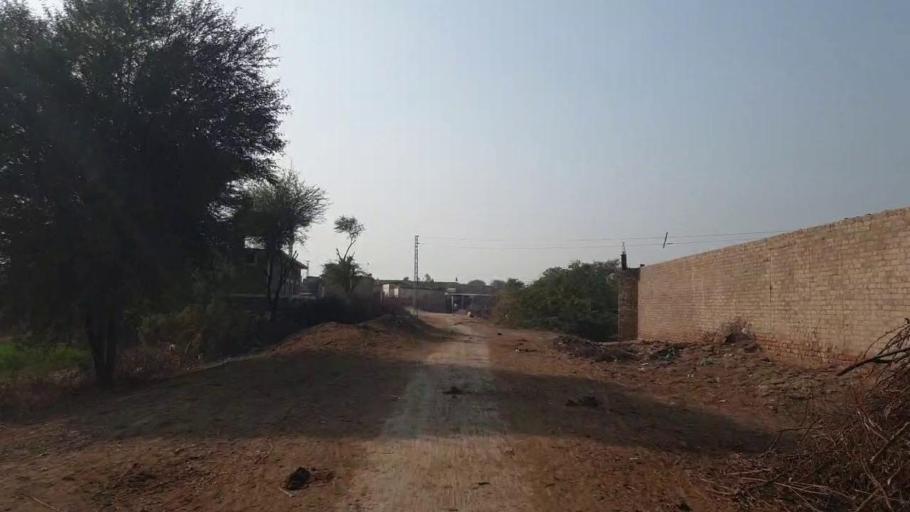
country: PK
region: Sindh
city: Shahdadpur
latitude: 26.0004
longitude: 68.5395
